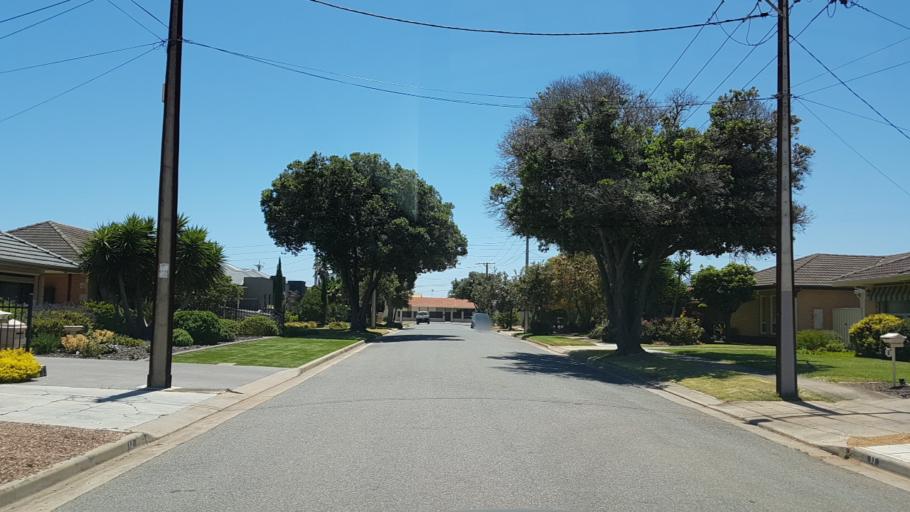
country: AU
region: South Australia
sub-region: Charles Sturt
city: West Lakes Shore
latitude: -34.8585
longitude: 138.4845
